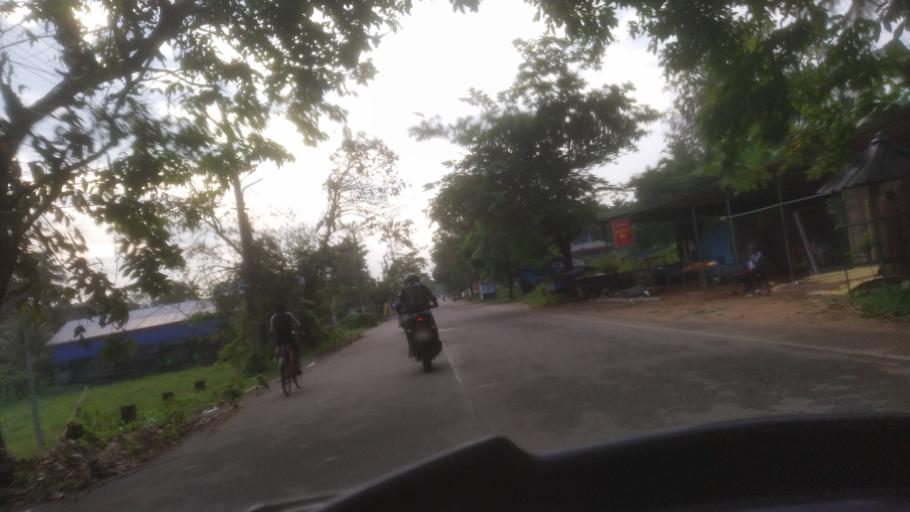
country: IN
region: Kerala
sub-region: Ernakulam
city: Kotamangalam
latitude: 10.0674
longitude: 76.6299
